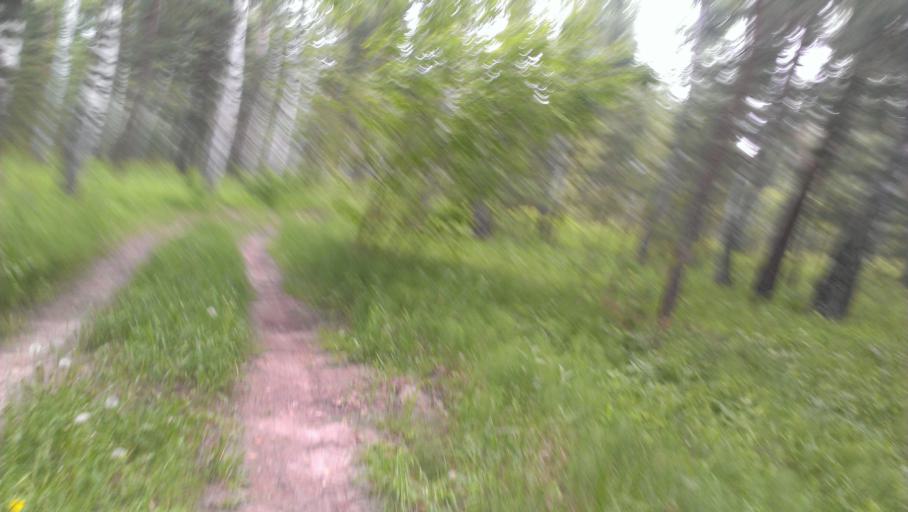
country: RU
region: Altai Krai
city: Sannikovo
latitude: 53.3470
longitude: 84.0407
